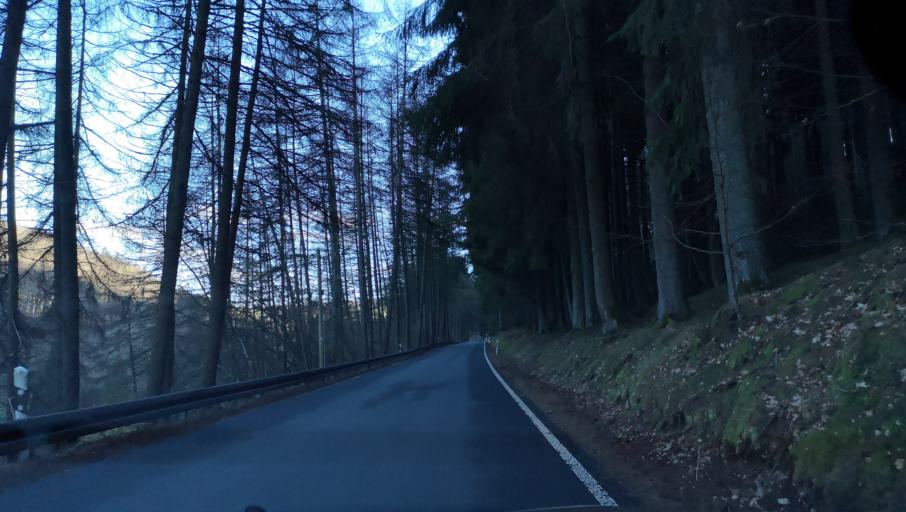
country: DE
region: North Rhine-Westphalia
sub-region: Regierungsbezirk Arnsberg
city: Breckerfeld
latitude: 51.2636
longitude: 7.4134
